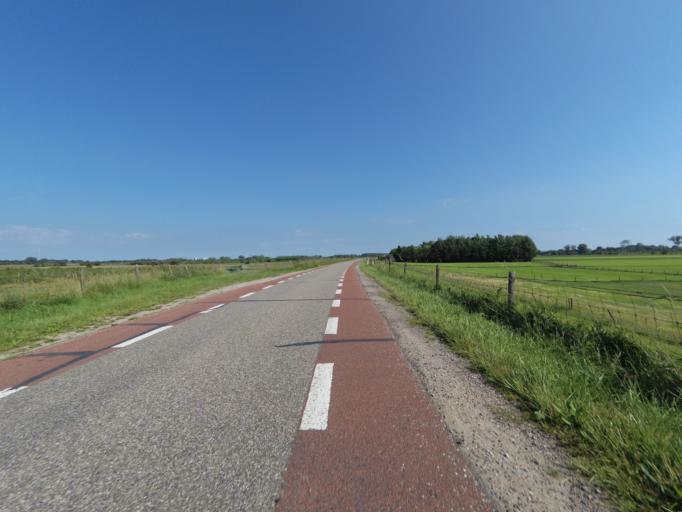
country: NL
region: Utrecht
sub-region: Gemeente Houten
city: Houten
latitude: 51.9768
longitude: 5.1534
